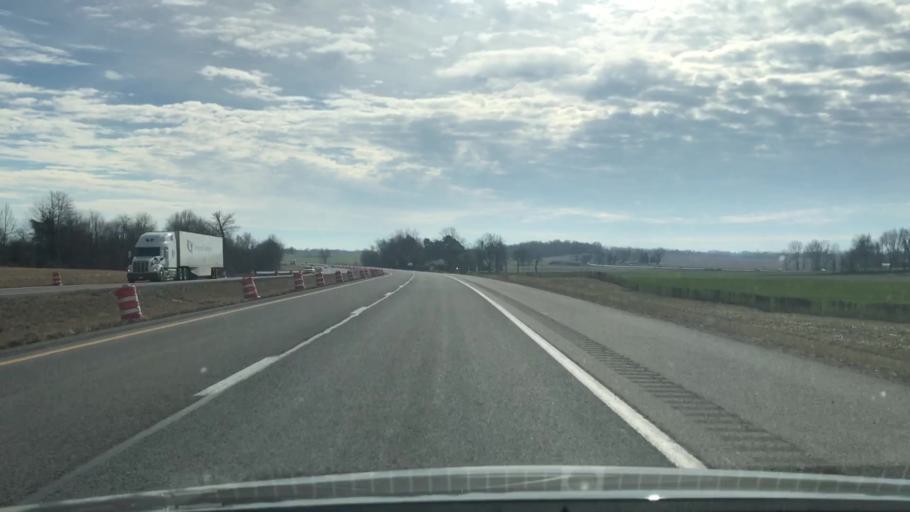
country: US
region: Kentucky
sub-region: Daviess County
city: Masonville
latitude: 37.6735
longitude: -87.0268
